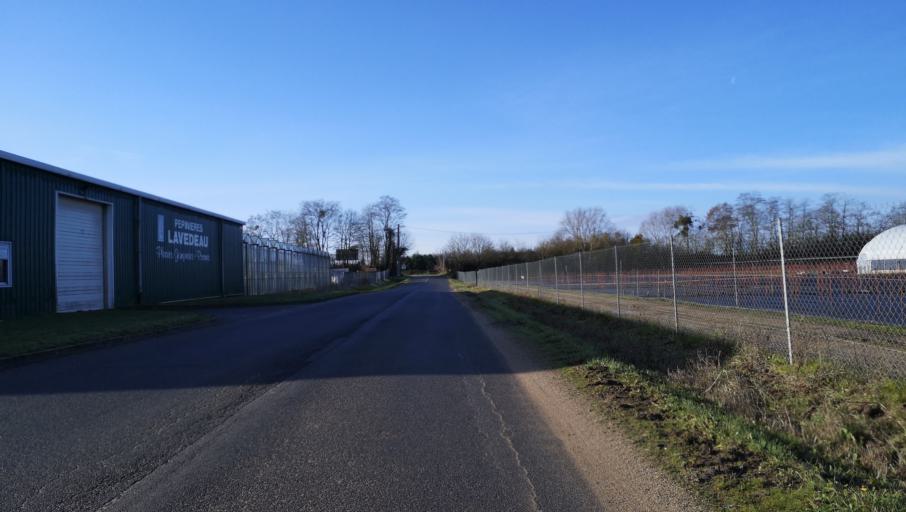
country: FR
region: Centre
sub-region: Departement du Loiret
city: Saint-Denis-en-Val
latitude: 47.8805
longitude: 1.9813
